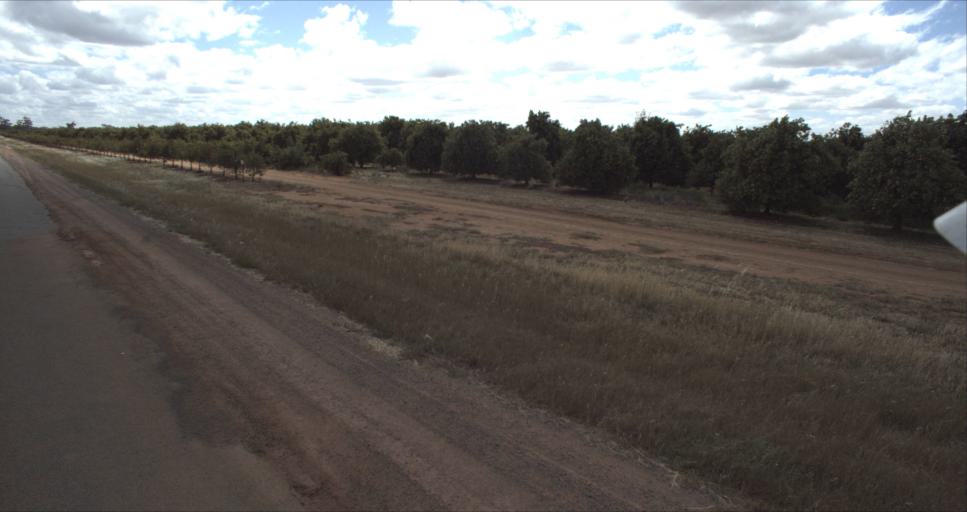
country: AU
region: New South Wales
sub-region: Leeton
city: Leeton
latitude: -34.5886
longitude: 146.3841
